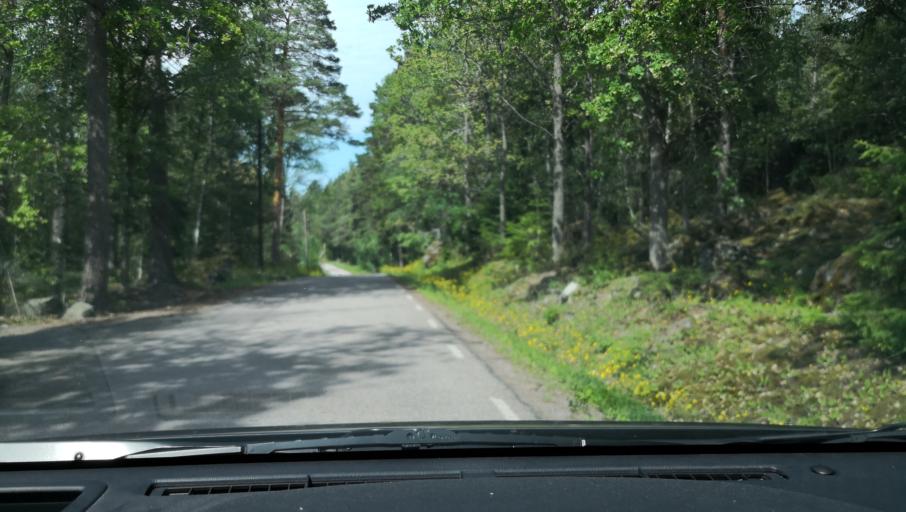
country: SE
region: Stockholm
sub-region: Sigtuna Kommun
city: Sigtuna
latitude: 59.6943
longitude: 17.6442
